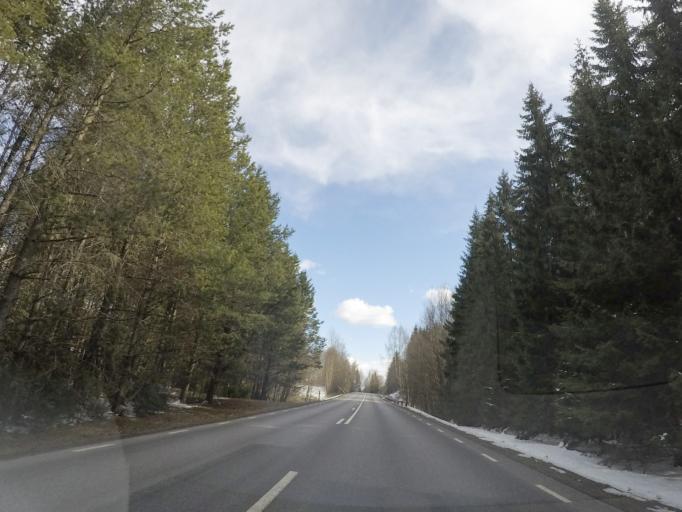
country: SE
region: Vaestmanland
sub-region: Skinnskattebergs Kommun
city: Skinnskatteberg
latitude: 59.8643
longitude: 15.6524
